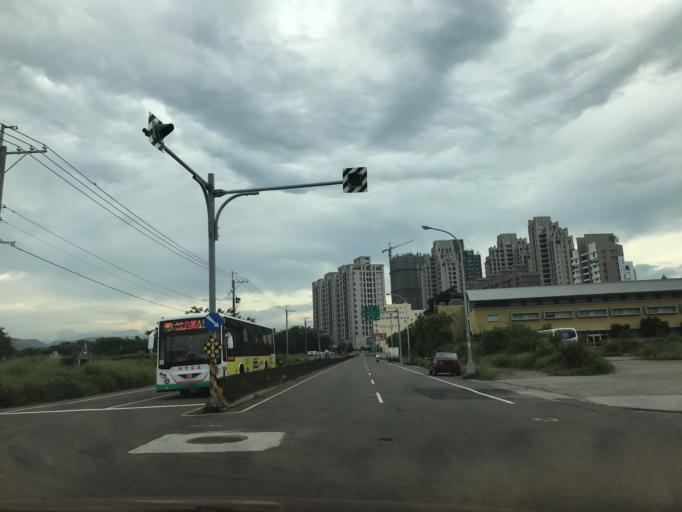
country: TW
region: Taiwan
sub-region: Hsinchu
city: Zhubei
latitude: 24.8167
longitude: 121.0329
